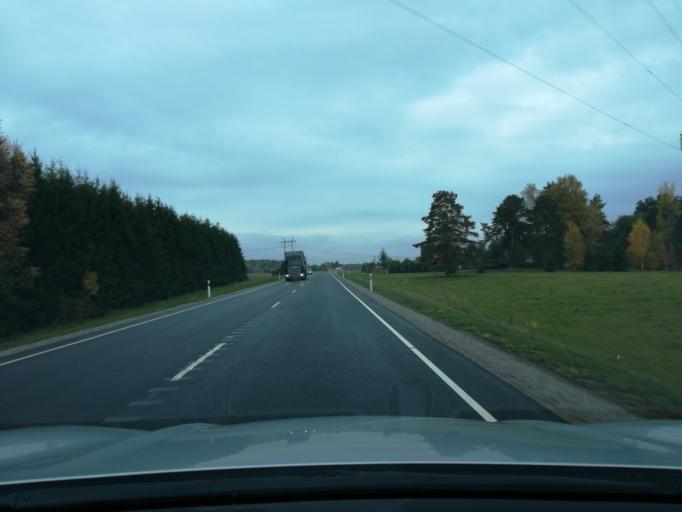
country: EE
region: Ida-Virumaa
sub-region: Johvi vald
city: Johvi
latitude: 59.0782
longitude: 27.3155
